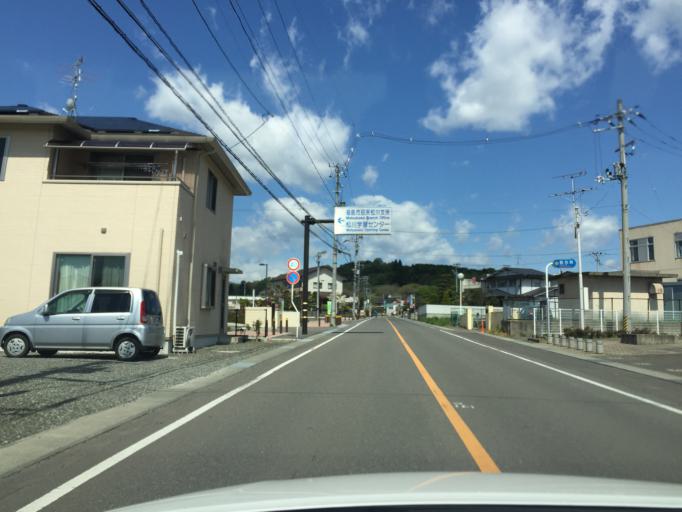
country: JP
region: Fukushima
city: Nihommatsu
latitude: 37.6582
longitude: 140.4690
